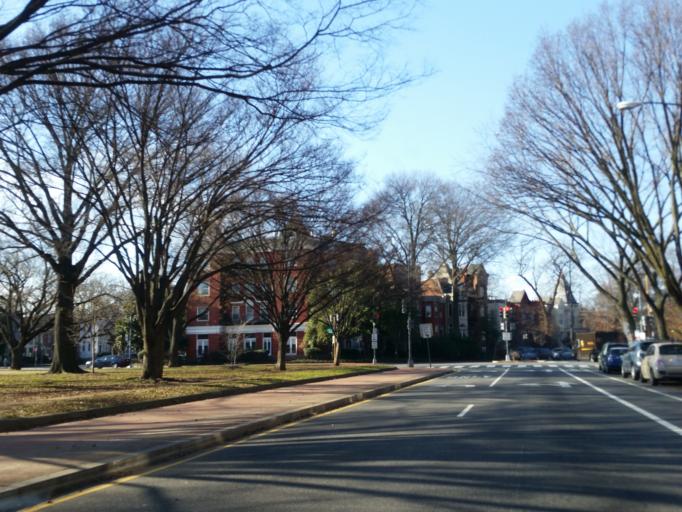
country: US
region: Washington, D.C.
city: Washington, D.C.
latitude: 38.8904
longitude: -76.9908
